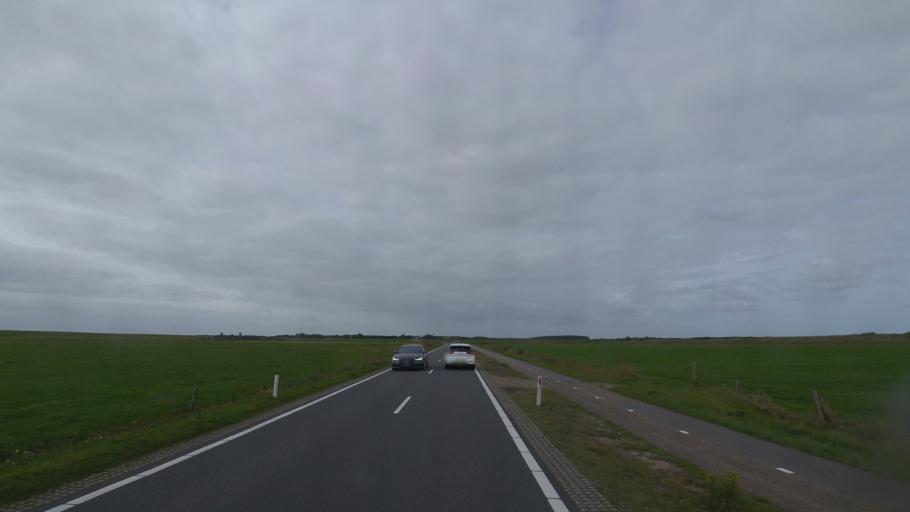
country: NL
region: Friesland
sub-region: Gemeente Ameland
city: Nes
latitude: 53.4460
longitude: 5.7421
